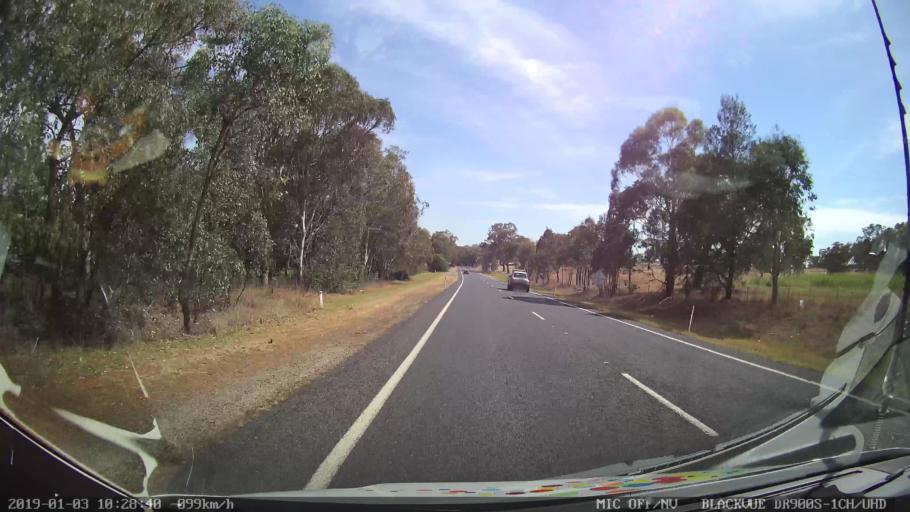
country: AU
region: New South Wales
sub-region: Young
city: Young
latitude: -34.3848
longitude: 148.2594
